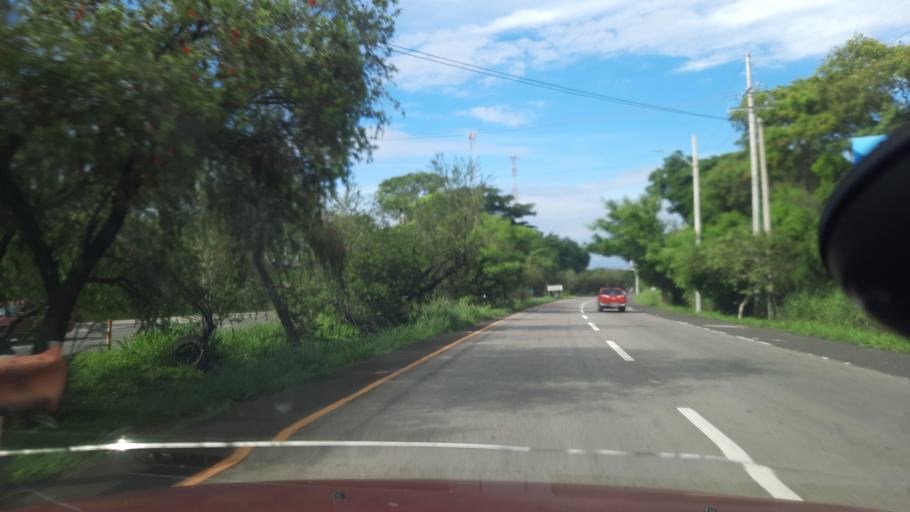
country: SV
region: La Paz
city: Olocuilta
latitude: 13.5372
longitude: -89.1113
